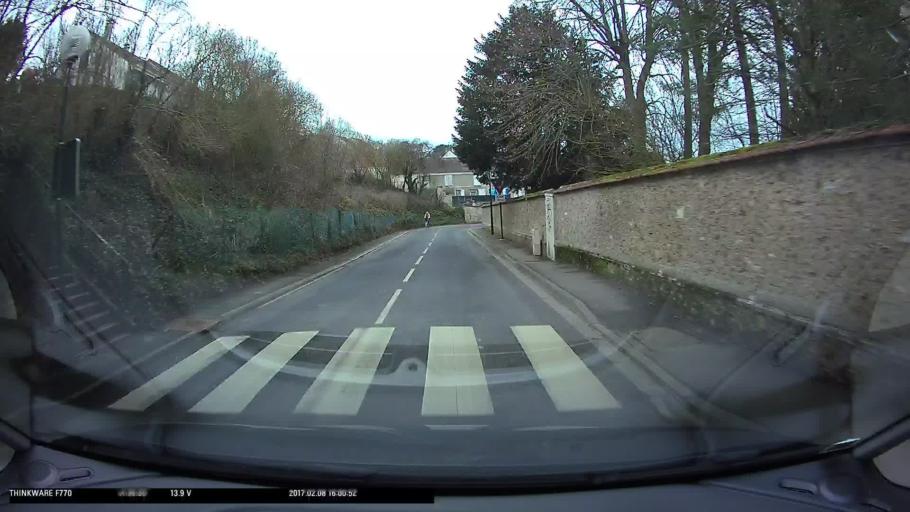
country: FR
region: Ile-de-France
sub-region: Departement du Val-d'Oise
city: Us
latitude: 49.1012
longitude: 1.9652
